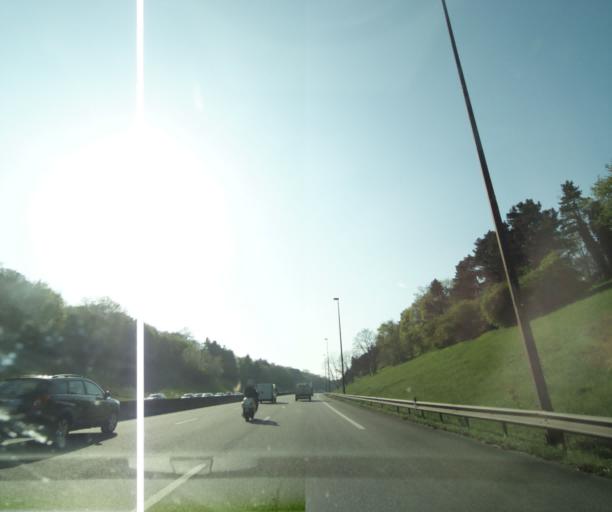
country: FR
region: Ile-de-France
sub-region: Departement des Hauts-de-Seine
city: Chatenay-Malabry
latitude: 48.7604
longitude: 2.2597
